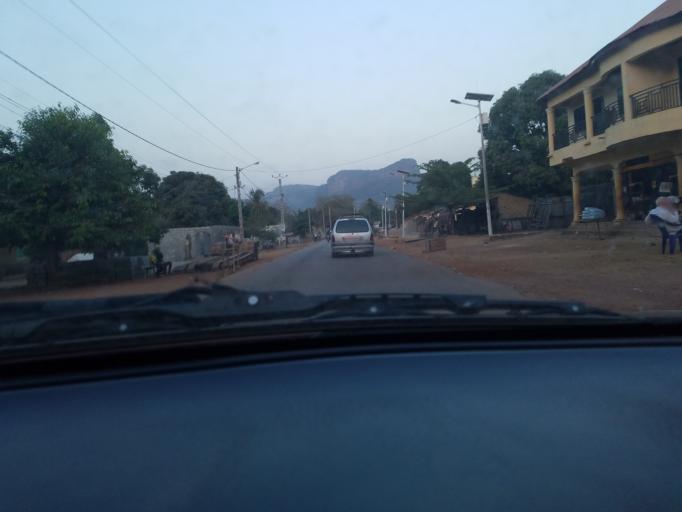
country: GN
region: Kindia
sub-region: Prefecture de Dubreka
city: Dubreka
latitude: 9.7889
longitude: -13.5064
